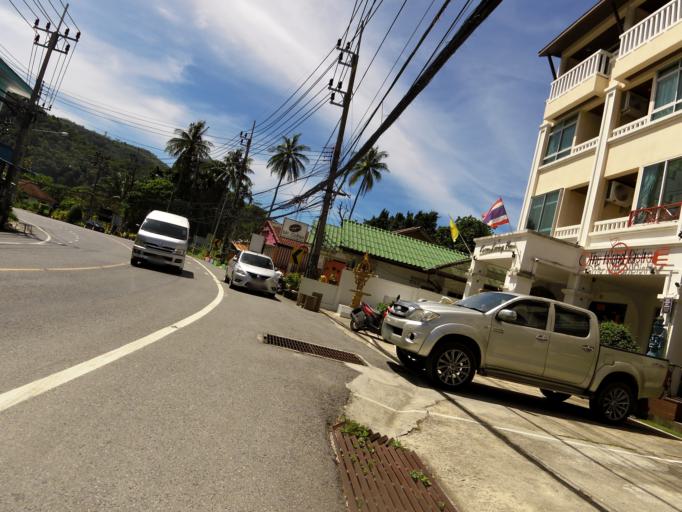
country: TH
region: Phuket
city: Ban Karon
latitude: 7.8453
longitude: 98.2990
